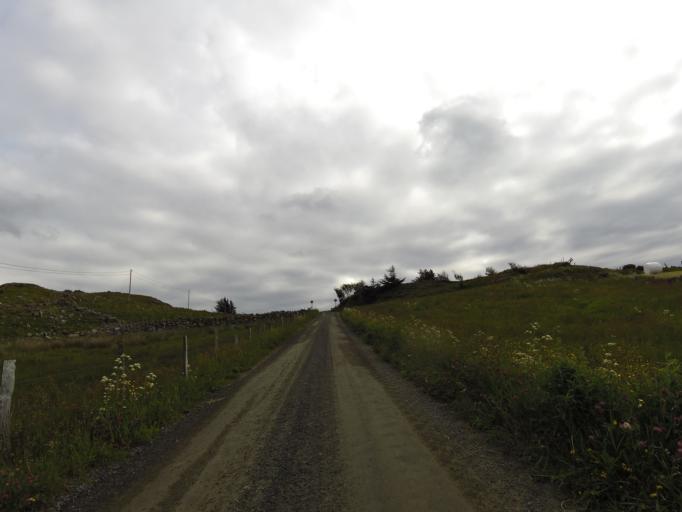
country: NO
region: Vest-Agder
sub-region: Farsund
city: Vestbygd
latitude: 58.1415
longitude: 6.6110
